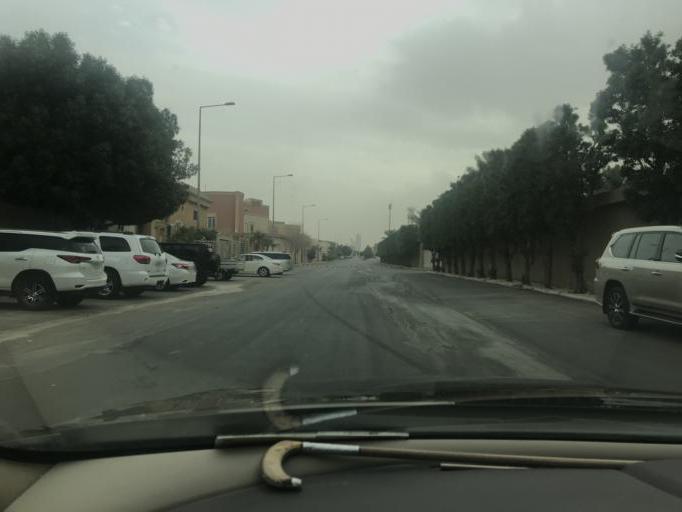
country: SA
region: Ar Riyad
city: Riyadh
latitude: 24.7885
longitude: 46.7007
